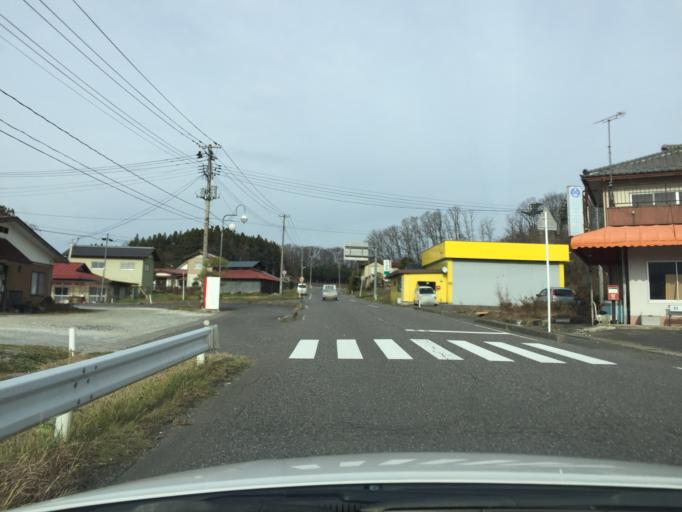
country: JP
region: Fukushima
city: Funehikimachi-funehiki
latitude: 37.3945
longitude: 140.5922
